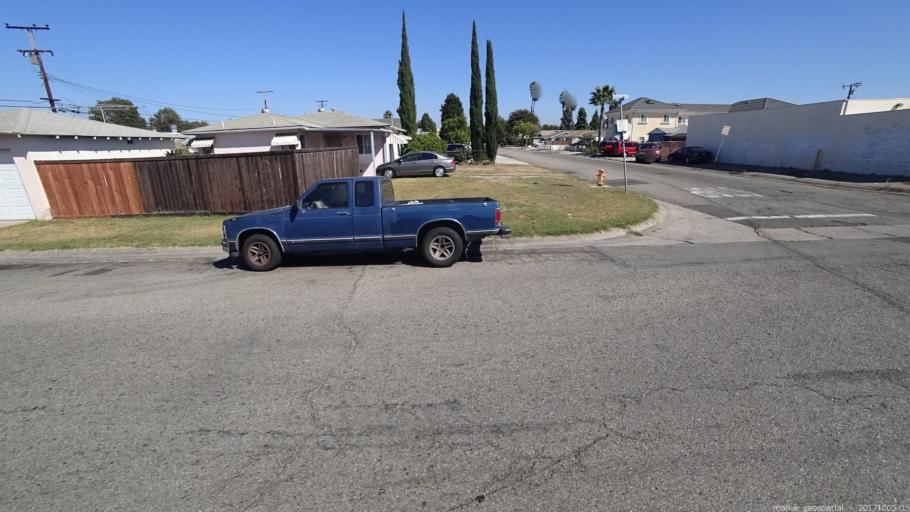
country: US
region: California
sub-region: Orange County
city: Garden Grove
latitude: 33.7753
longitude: -117.9475
